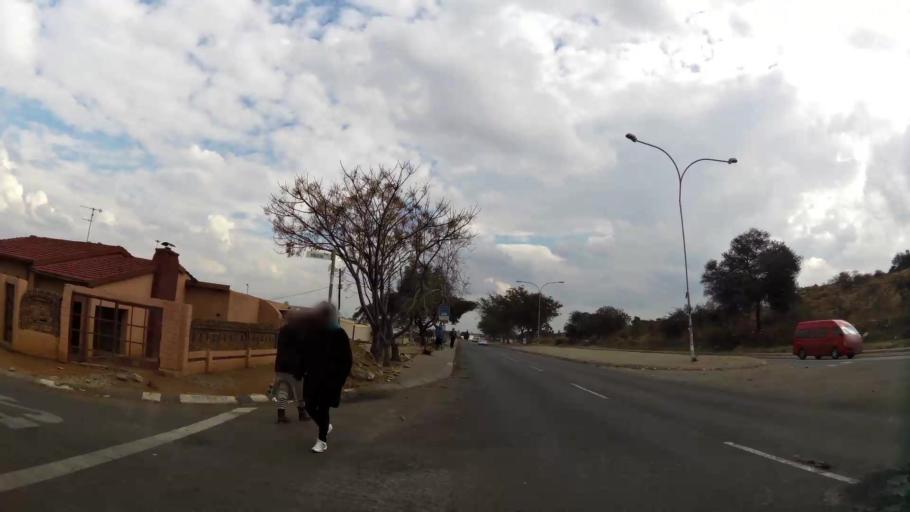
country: ZA
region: Gauteng
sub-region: City of Johannesburg Metropolitan Municipality
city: Soweto
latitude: -26.2337
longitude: 27.8712
